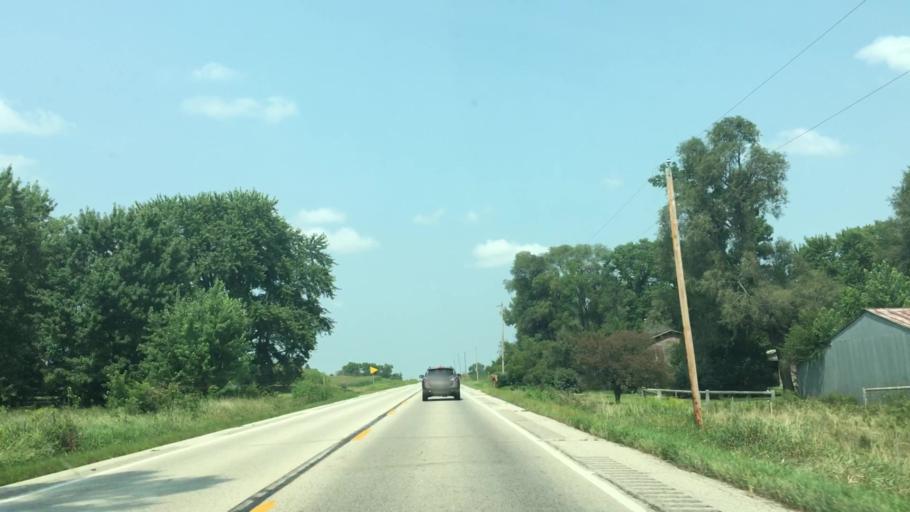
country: US
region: Iowa
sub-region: Buchanan County
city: Independence
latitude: 42.5296
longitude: -91.8899
